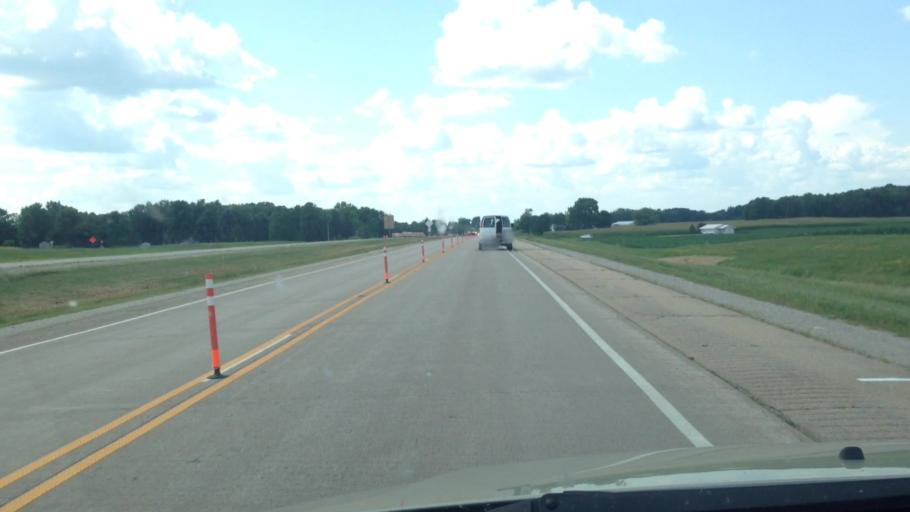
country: US
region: Wisconsin
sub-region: Brown County
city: Pulaski
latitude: 44.6924
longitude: -88.3351
